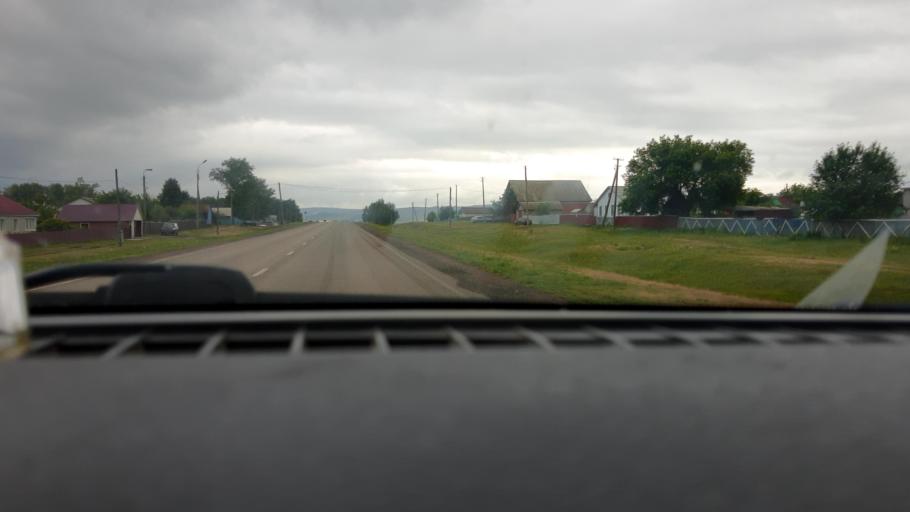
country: RU
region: Bashkortostan
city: Serafimovskiy
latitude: 54.4445
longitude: 53.9746
